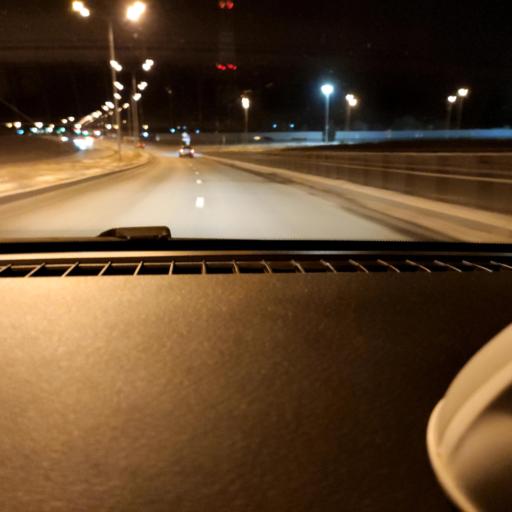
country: RU
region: Samara
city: Samara
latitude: 53.2894
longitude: 50.2305
